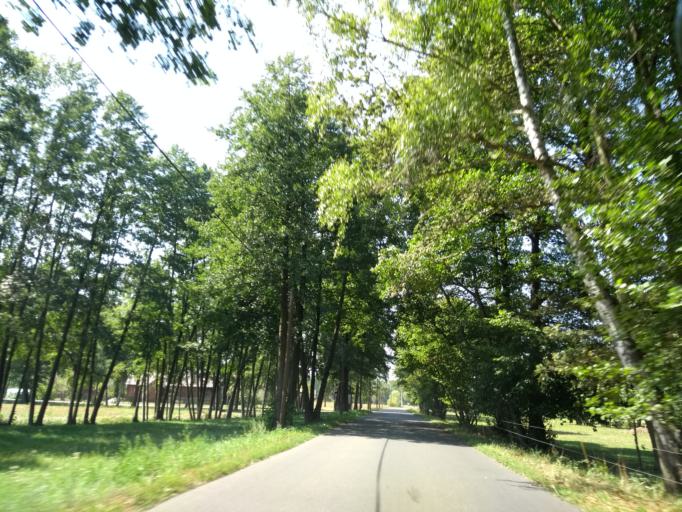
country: DE
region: Brandenburg
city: Burg
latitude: 51.8517
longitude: 14.1185
